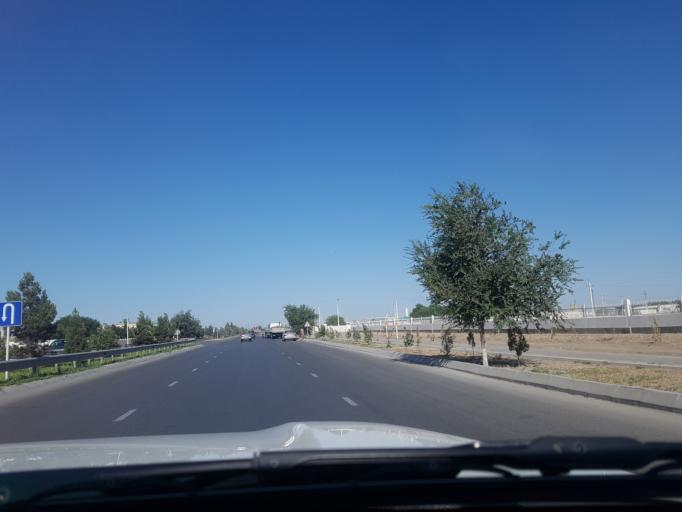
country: TM
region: Lebap
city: Turkmenabat
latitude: 38.9961
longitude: 63.5403
